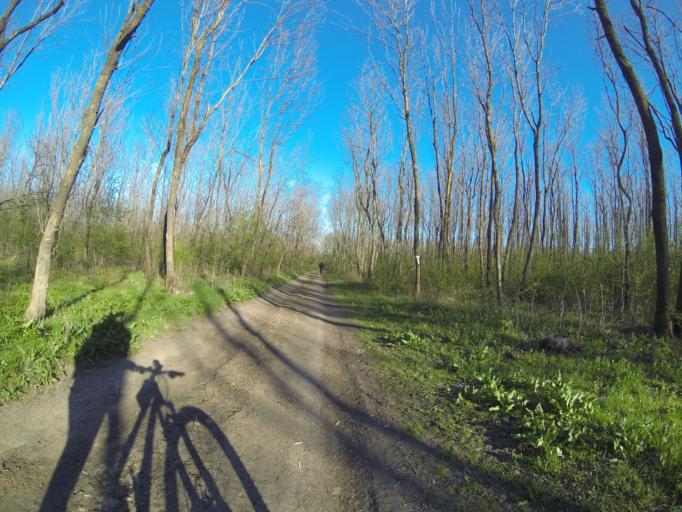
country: RO
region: Dolj
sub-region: Comuna Ceratu
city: Ceratu
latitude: 44.0829
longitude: 23.6806
